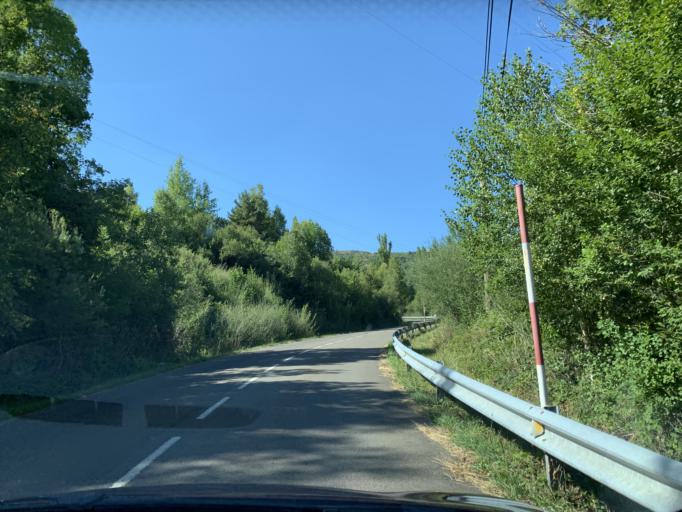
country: ES
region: Aragon
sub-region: Provincia de Huesca
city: Hoz de Jaca
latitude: 42.7021
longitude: -0.3207
